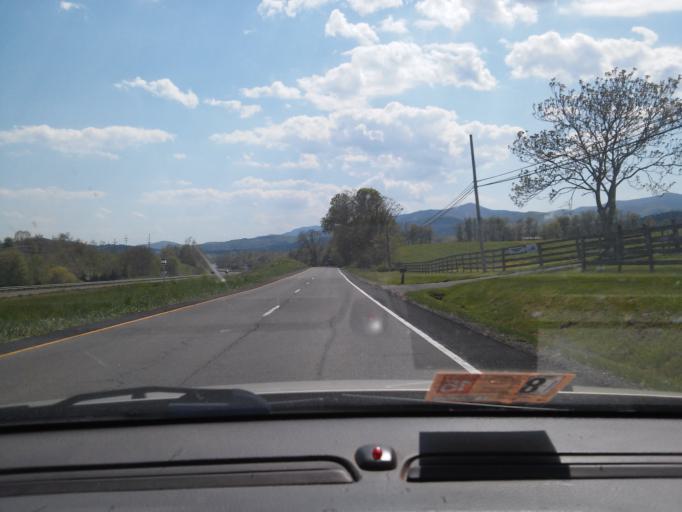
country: US
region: Virginia
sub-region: Rappahannock County
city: Washington
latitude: 38.6736
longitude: -78.2125
